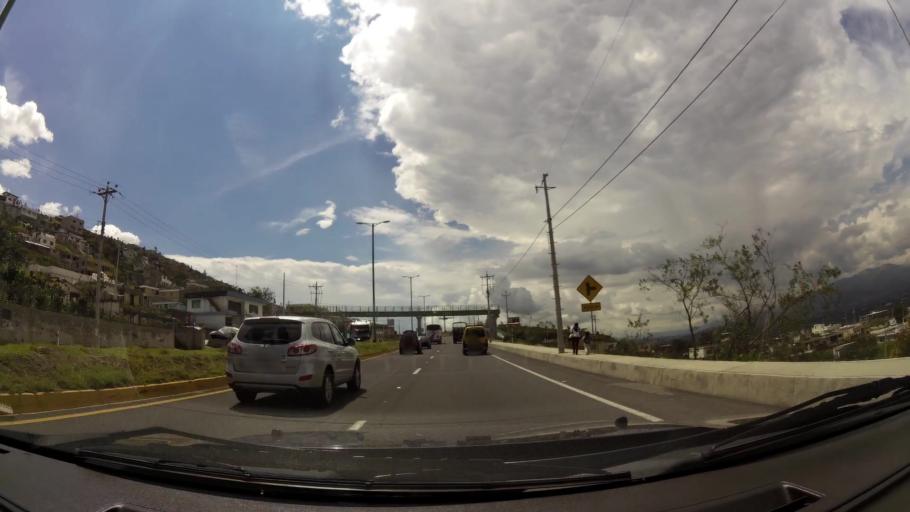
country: EC
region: Pichincha
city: Quito
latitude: -0.0959
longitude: -78.4097
